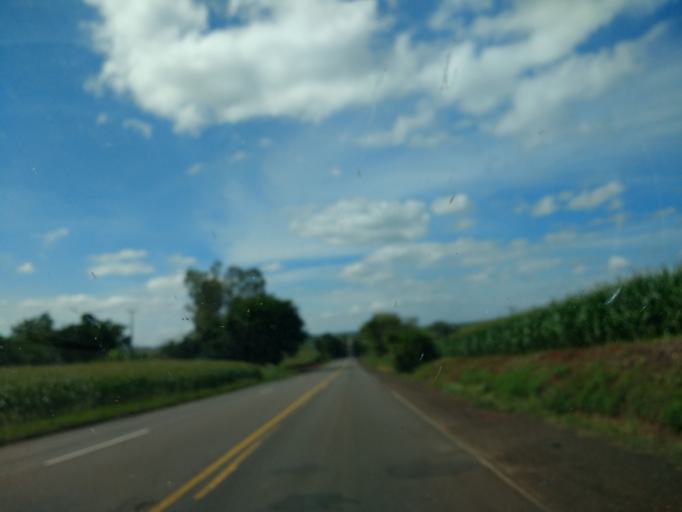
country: BR
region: Parana
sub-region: Terra Boa
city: Terra Boa
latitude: -23.6004
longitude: -52.3992
